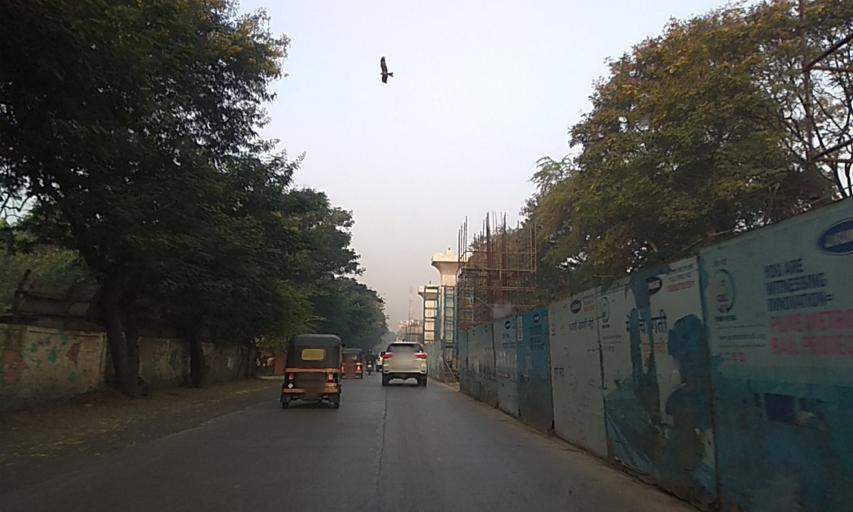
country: IN
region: Maharashtra
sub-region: Pune Division
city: Shivaji Nagar
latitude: 18.5301
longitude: 73.8671
